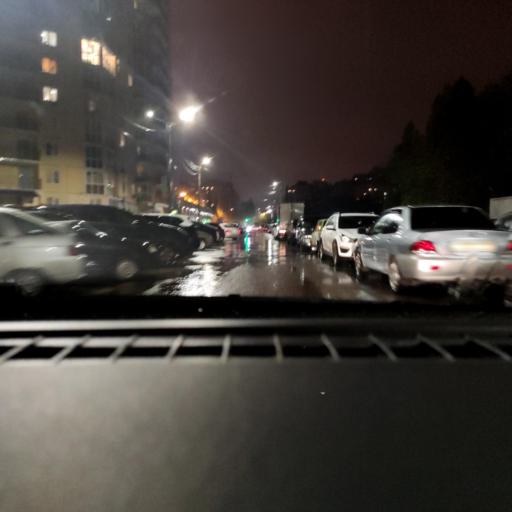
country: RU
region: Voronezj
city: Voronezh
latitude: 51.7036
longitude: 39.2006
